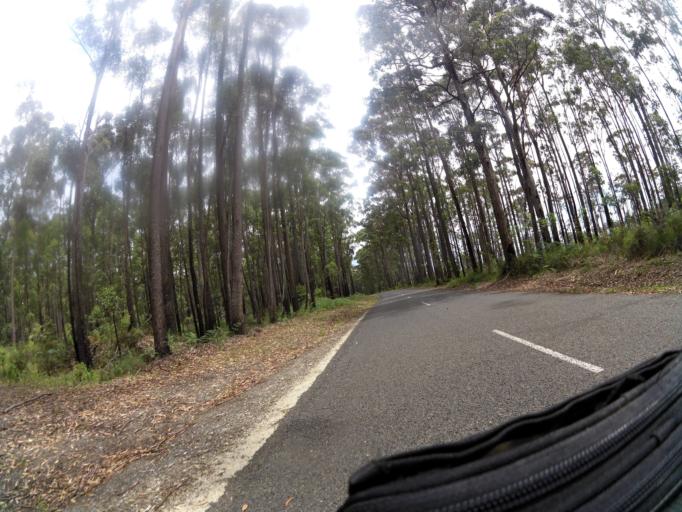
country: AU
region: Victoria
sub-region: East Gippsland
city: Lakes Entrance
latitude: -37.7045
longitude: 148.7358
